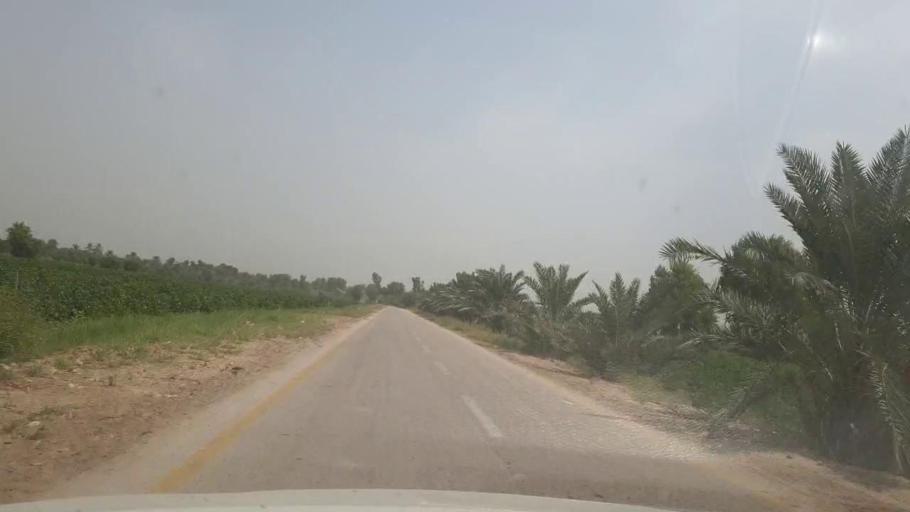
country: PK
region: Sindh
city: Kot Diji
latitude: 27.3774
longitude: 68.6529
